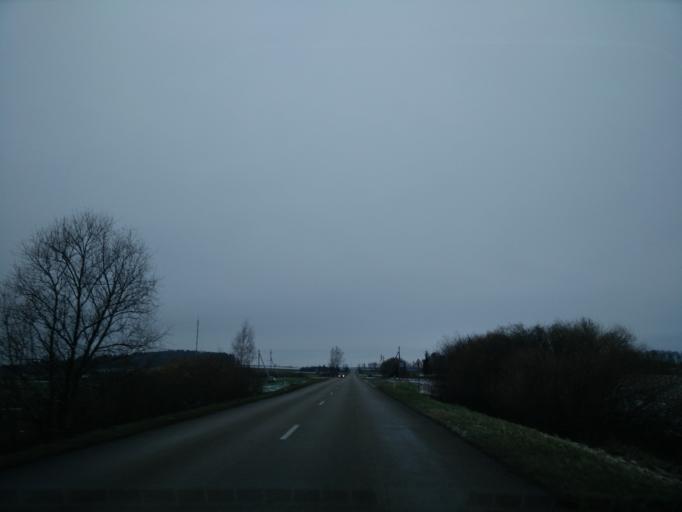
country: LT
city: Ariogala
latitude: 55.3407
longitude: 23.3964
